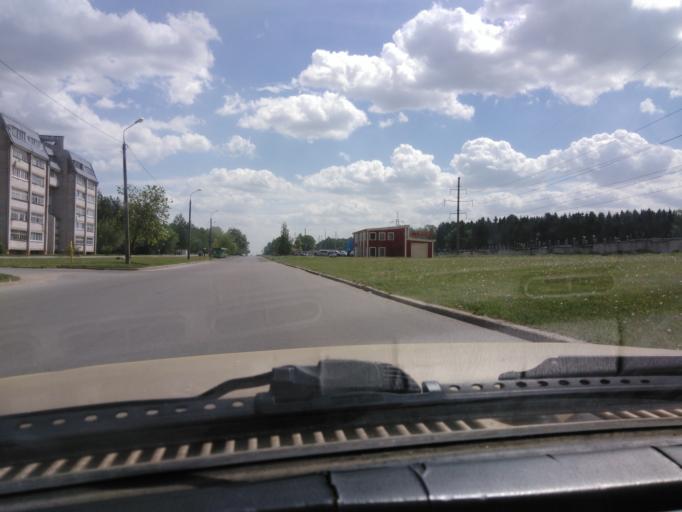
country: BY
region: Mogilev
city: Mahilyow
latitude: 53.9490
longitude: 30.3484
